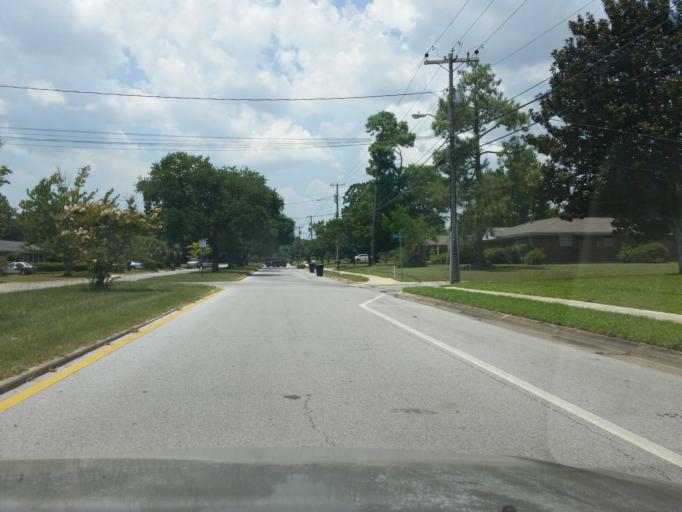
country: US
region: Florida
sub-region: Escambia County
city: East Pensacola Heights
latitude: 30.4560
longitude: -87.1700
